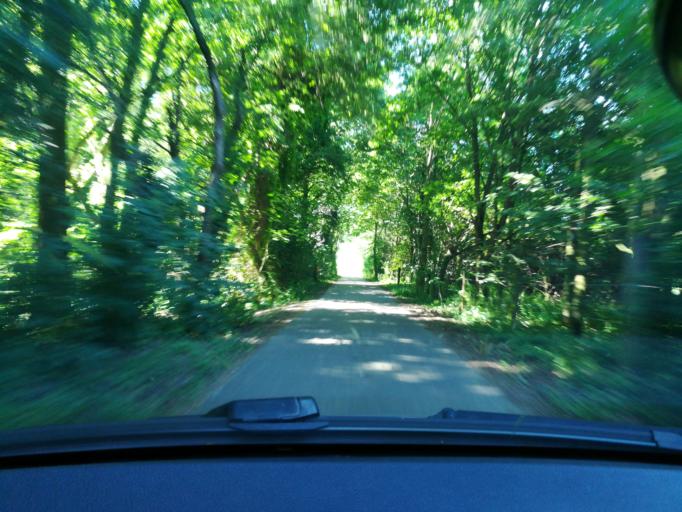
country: DE
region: North Rhine-Westphalia
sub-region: Regierungsbezirk Detmold
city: Minden
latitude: 52.3136
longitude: 8.9229
